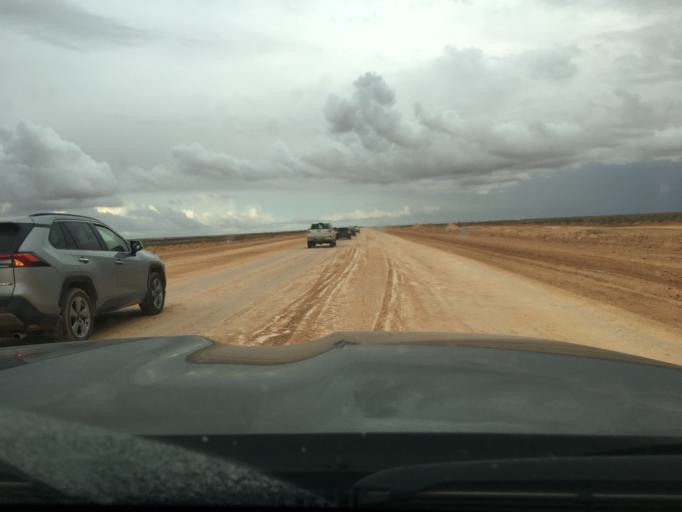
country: TN
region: Madanin
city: Medenine
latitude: 33.2729
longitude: 10.5888
